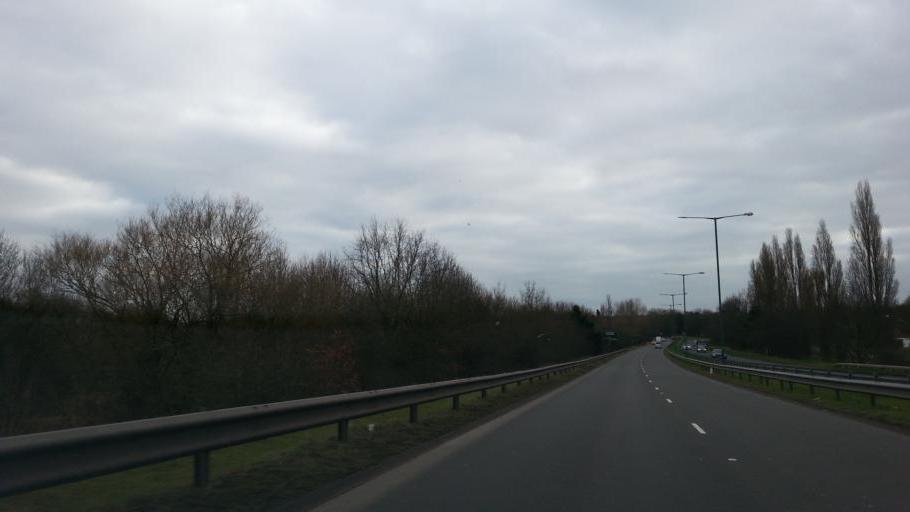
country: GB
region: England
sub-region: Solihull
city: Chelmsley Wood
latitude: 52.4898
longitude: -1.7344
